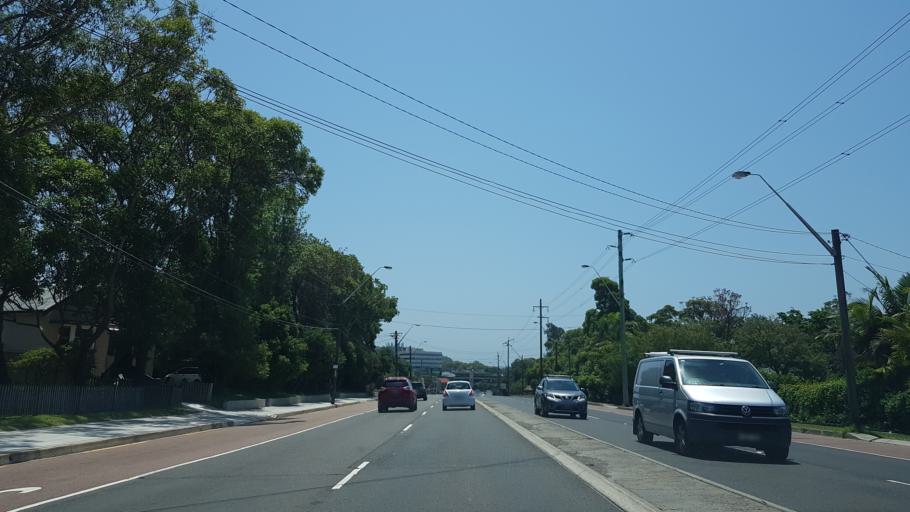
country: AU
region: New South Wales
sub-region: Pittwater
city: Warriewood
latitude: -33.6829
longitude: 151.3034
